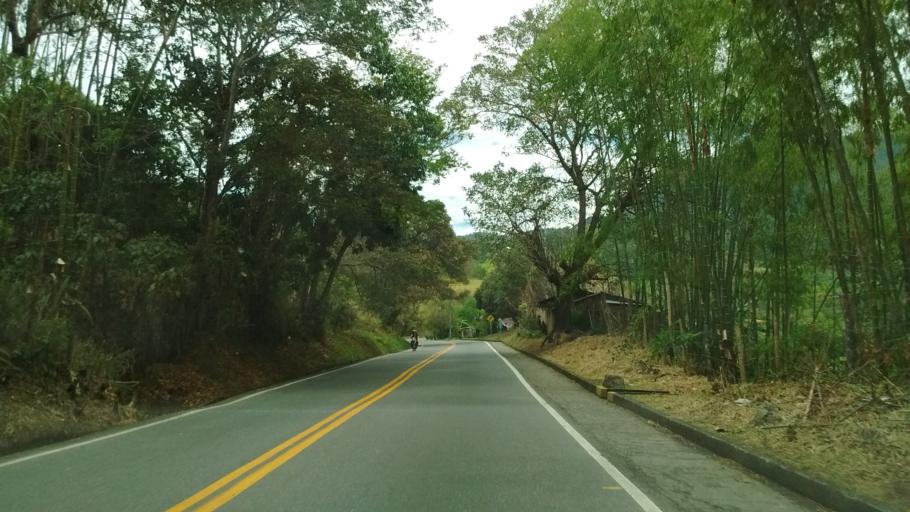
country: CO
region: Cauca
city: Rosas
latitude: 2.2330
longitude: -76.7866
